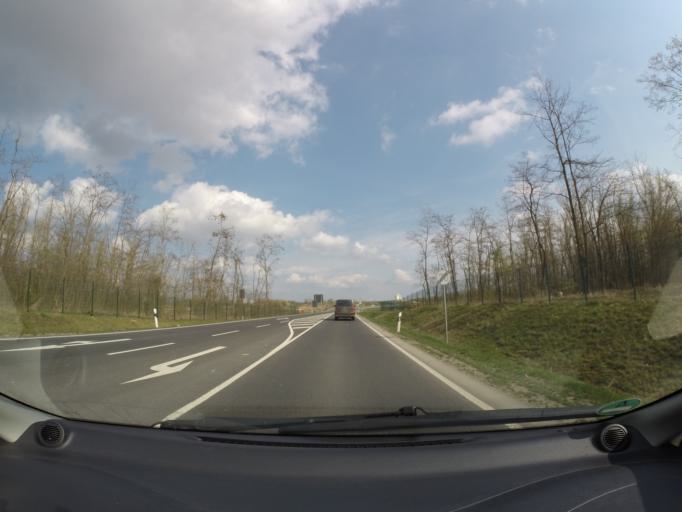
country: DE
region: Brandenburg
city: Rehfelde
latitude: 52.4885
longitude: 13.8486
